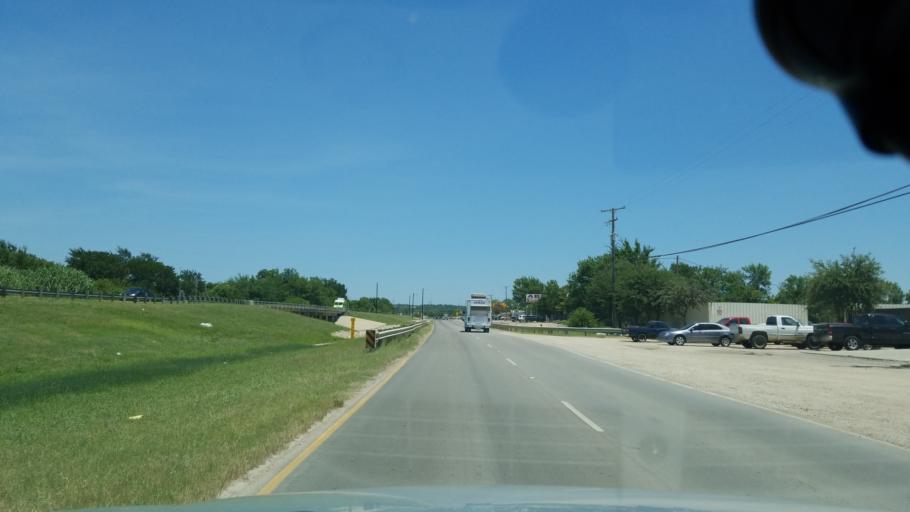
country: US
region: Texas
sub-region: Dallas County
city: Cockrell Hill
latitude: 32.7465
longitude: -96.9414
